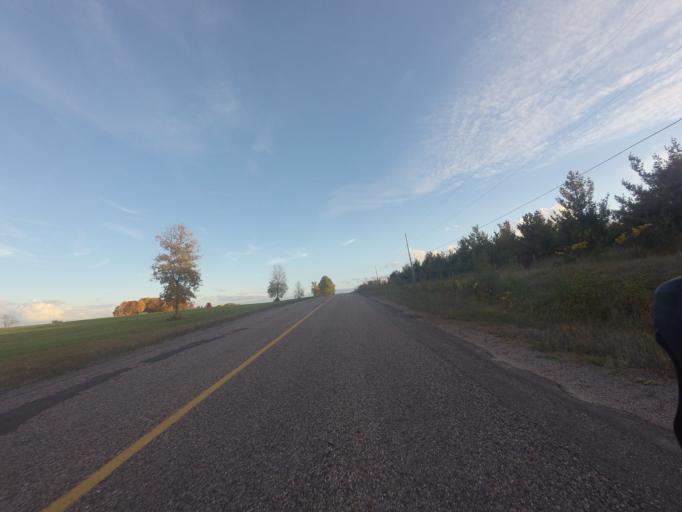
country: CA
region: Ontario
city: Renfrew
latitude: 45.4629
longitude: -76.9768
